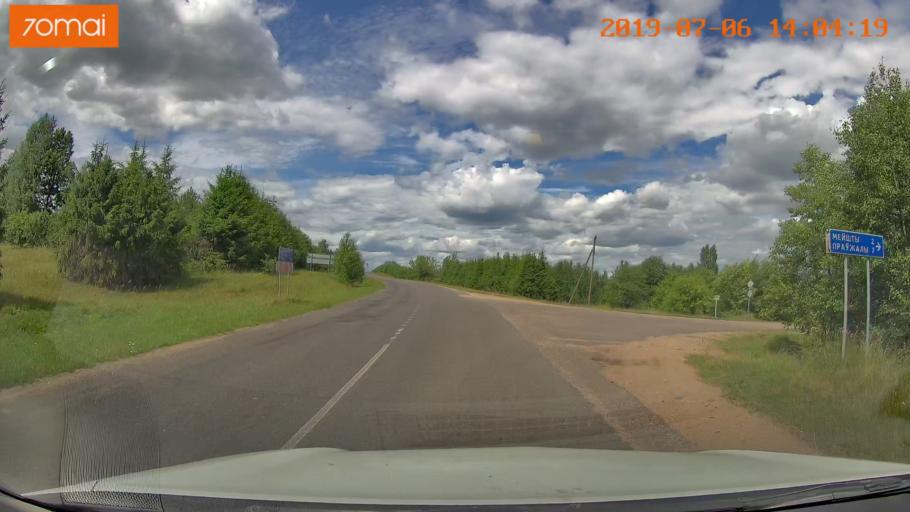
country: BY
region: Minsk
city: Ivyanyets
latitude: 53.8382
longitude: 26.8005
